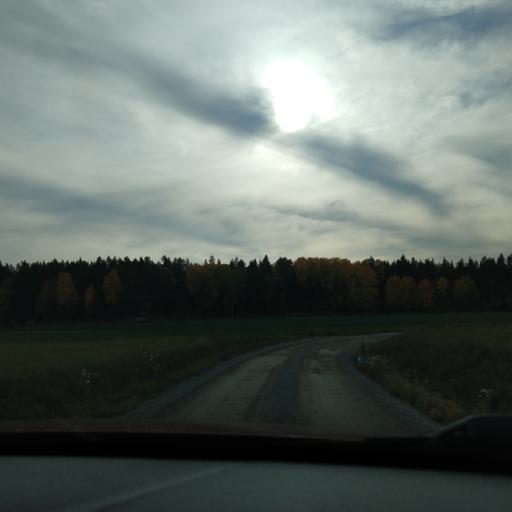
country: SE
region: Stockholm
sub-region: Vallentuna Kommun
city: Vallentuna
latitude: 59.5333
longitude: 18.0125
